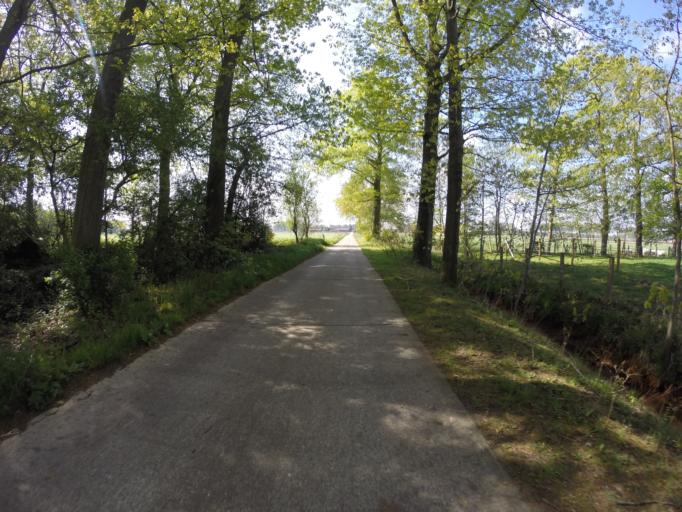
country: BE
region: Flanders
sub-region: Provincie West-Vlaanderen
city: Beernem
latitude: 51.0989
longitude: 3.3438
